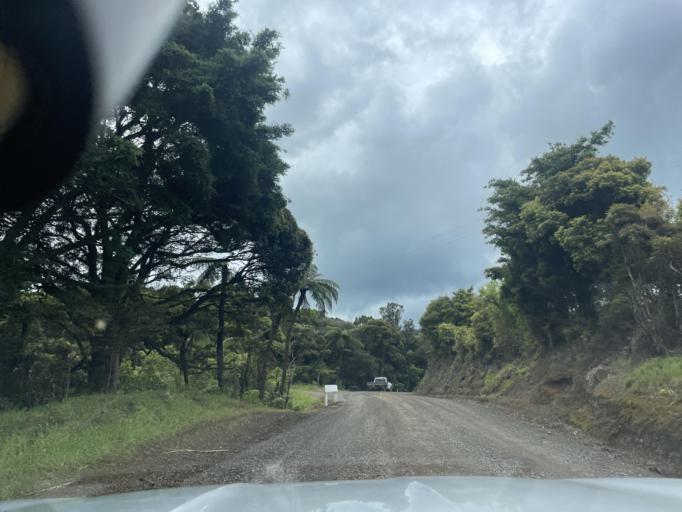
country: NZ
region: Northland
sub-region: Kaipara District
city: Dargaville
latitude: -35.7120
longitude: 173.6326
